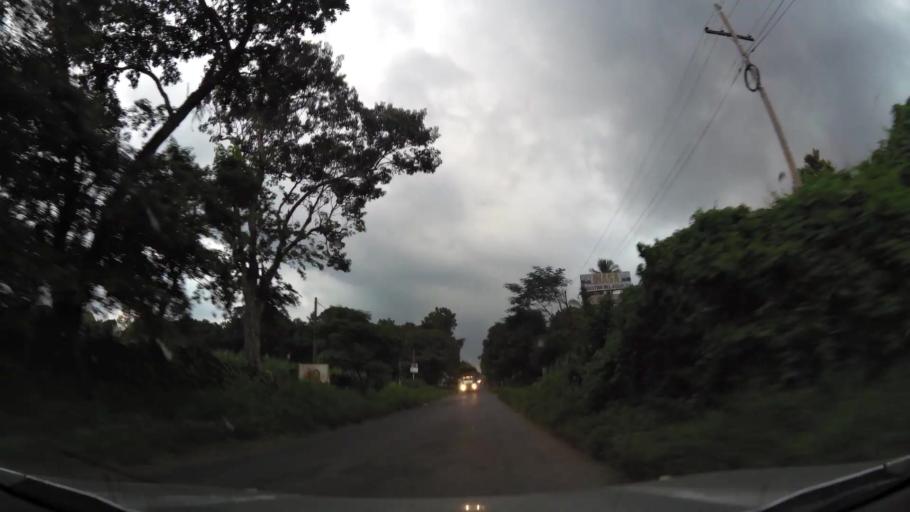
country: GT
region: Escuintla
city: Santa Lucia Cotzumalguapa
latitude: 14.3141
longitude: -91.0418
